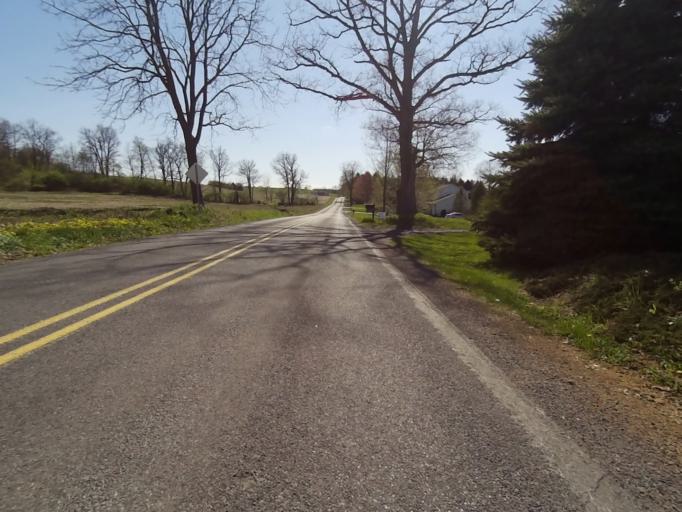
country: US
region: Pennsylvania
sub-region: Centre County
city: Houserville
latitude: 40.8784
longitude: -77.8255
